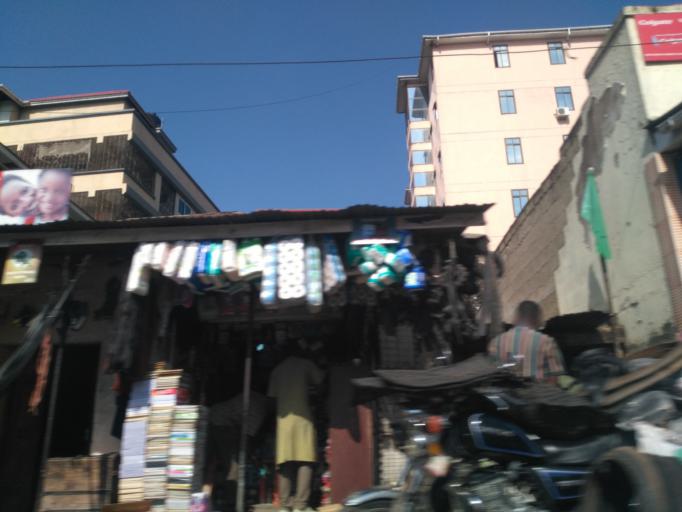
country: TZ
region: Arusha
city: Arusha
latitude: -3.3715
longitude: 36.6865
